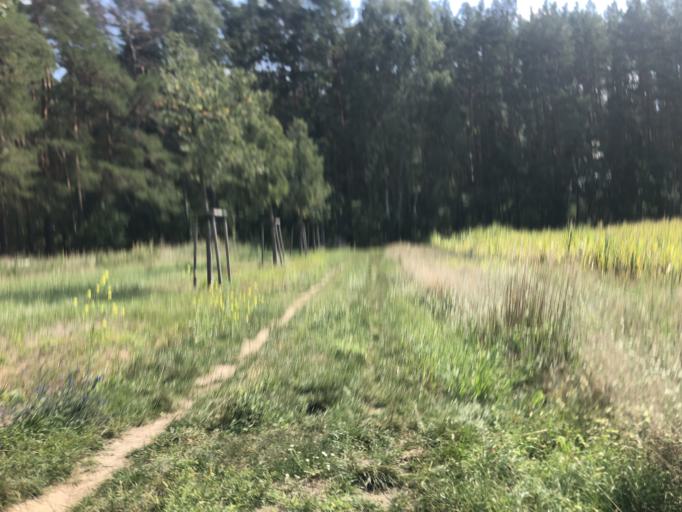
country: DE
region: Brandenburg
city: Mullrose
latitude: 52.2343
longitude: 14.4047
